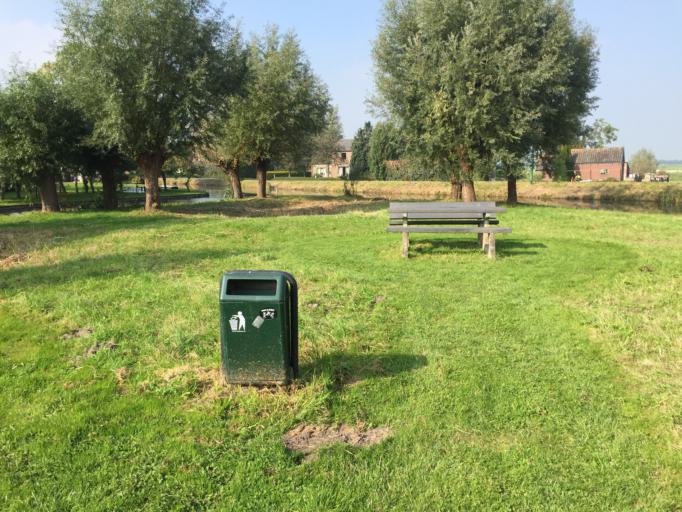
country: NL
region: Utrecht
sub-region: Gemeente Lopik
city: Lopik
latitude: 51.9749
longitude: 4.9254
